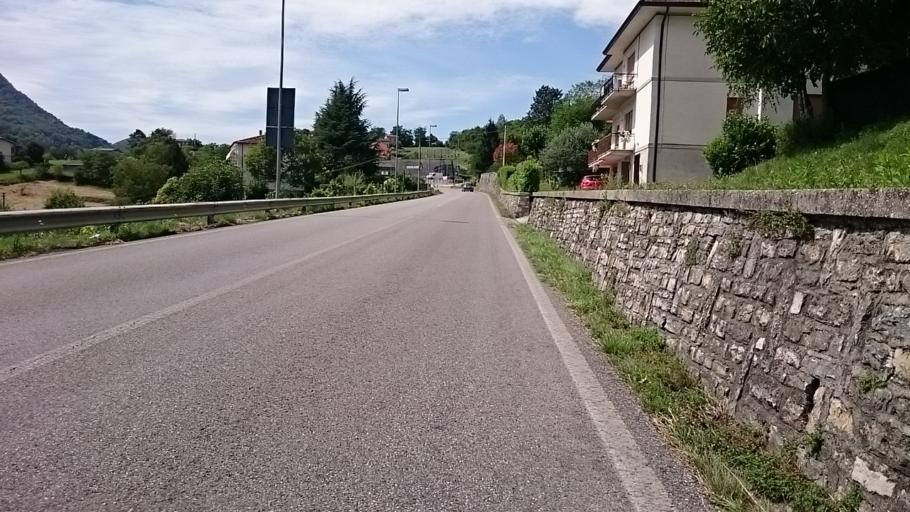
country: IT
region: Veneto
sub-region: Provincia di Treviso
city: Revine
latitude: 46.0050
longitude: 12.2677
